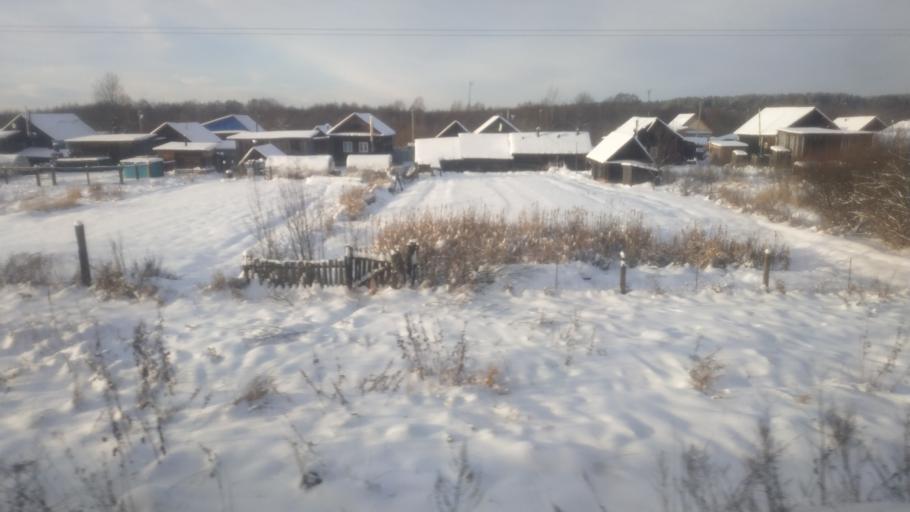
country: RU
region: Udmurtiya
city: Kizner
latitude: 56.2742
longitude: 51.4953
